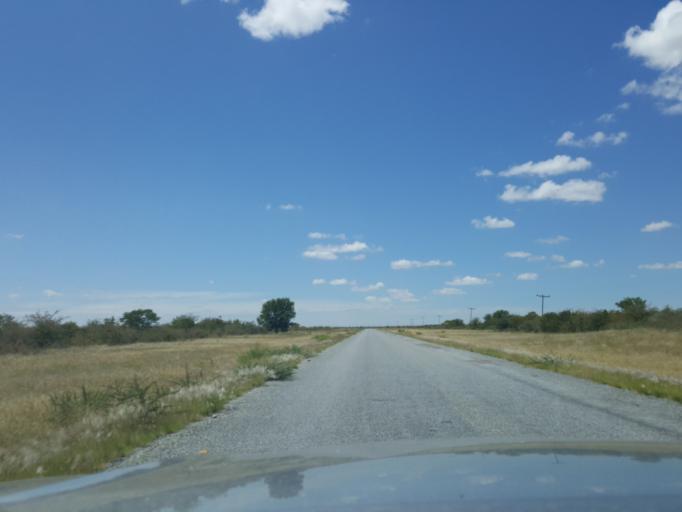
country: BW
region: Central
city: Gweta
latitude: -20.1377
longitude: 25.6648
